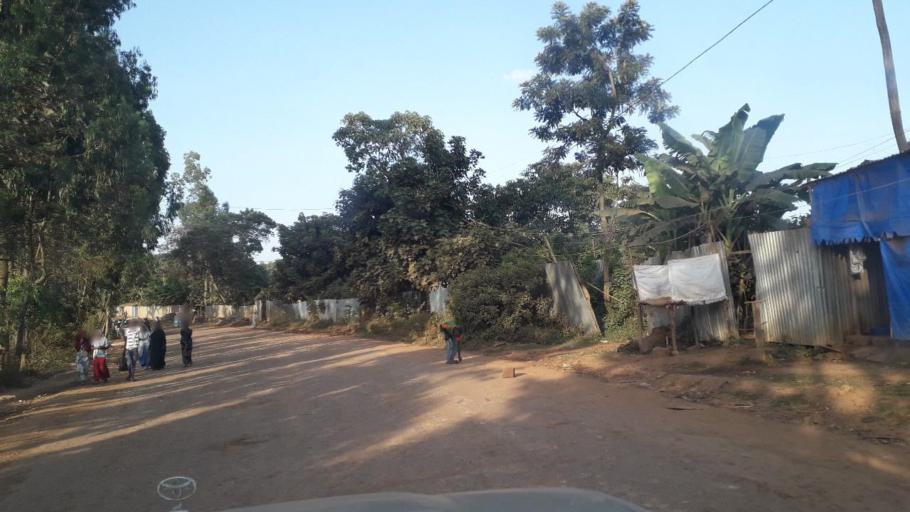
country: ET
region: Oromiya
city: Jima
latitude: 7.6353
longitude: 36.8356
